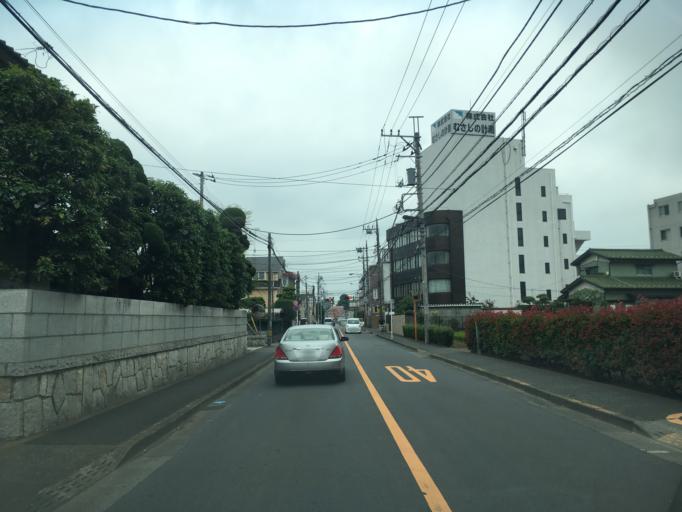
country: JP
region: Tokyo
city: Hino
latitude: 35.7307
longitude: 139.3988
